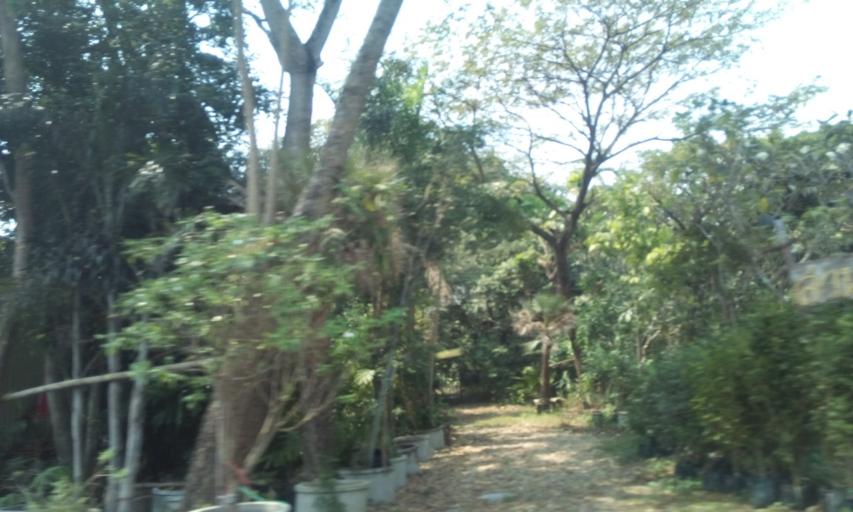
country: TH
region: Nakhon Nayok
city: Ongkharak
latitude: 14.1018
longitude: 100.9438
